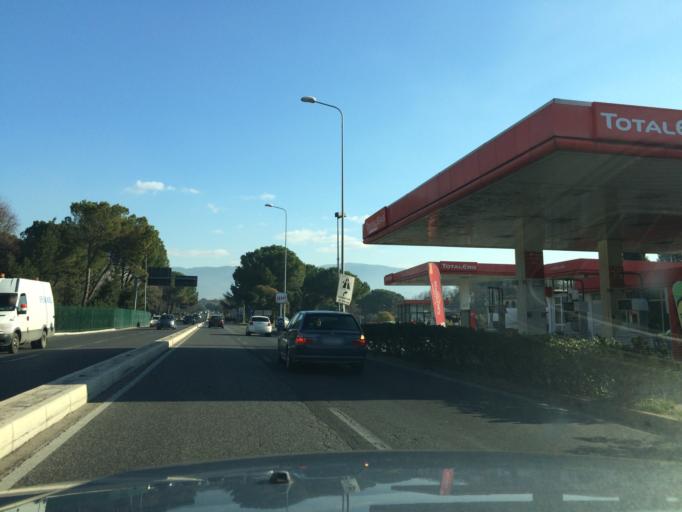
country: IT
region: Umbria
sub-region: Provincia di Terni
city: Terni
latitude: 42.5675
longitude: 12.6328
